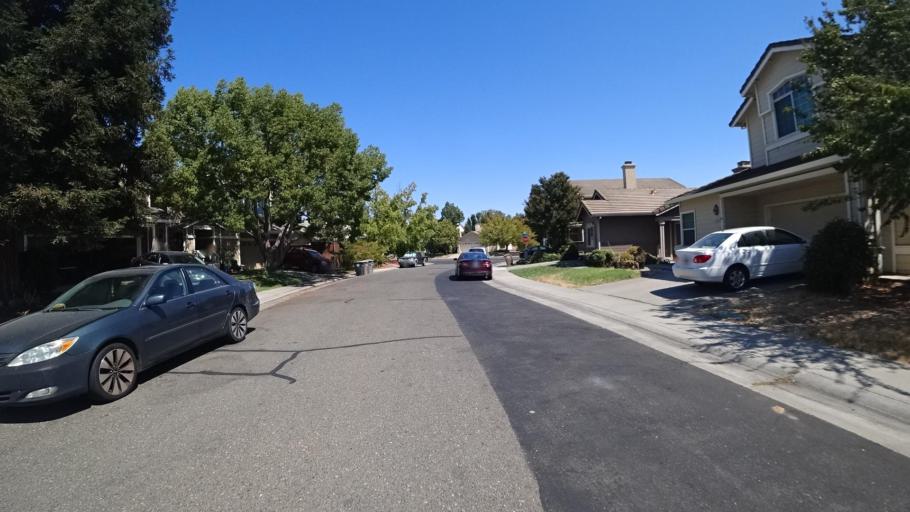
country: US
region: California
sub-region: Sacramento County
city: Laguna
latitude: 38.4211
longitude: -121.4132
